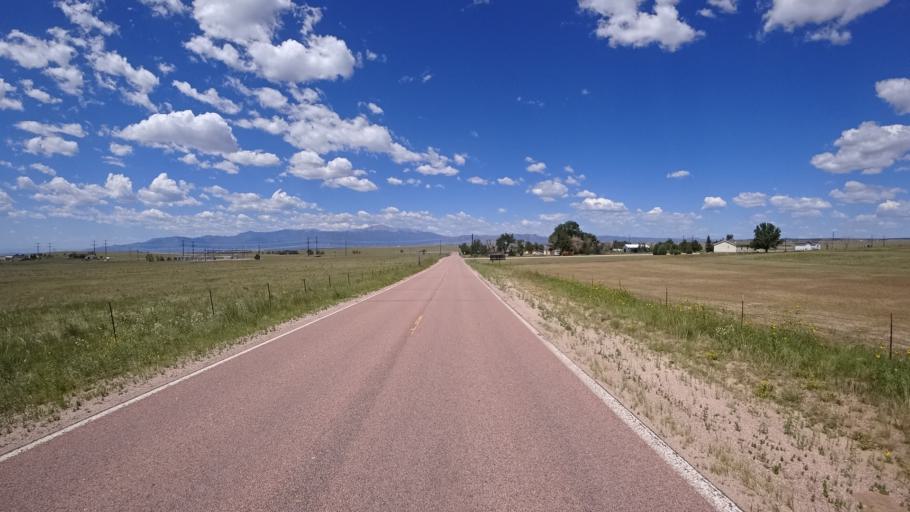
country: US
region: Colorado
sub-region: El Paso County
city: Cimarron Hills
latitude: 38.9116
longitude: -104.6206
